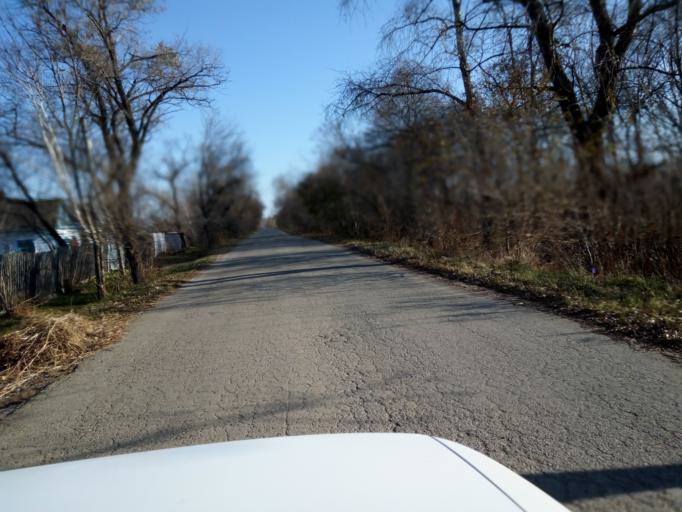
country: RU
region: Primorskiy
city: Lazo
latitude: 45.8820
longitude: 133.6484
